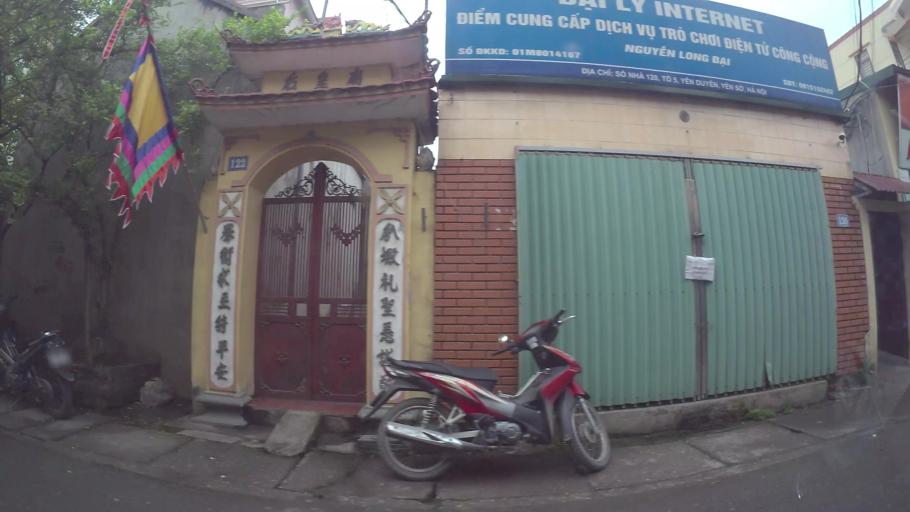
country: VN
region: Ha Noi
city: Van Dien
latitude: 20.9709
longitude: 105.8696
